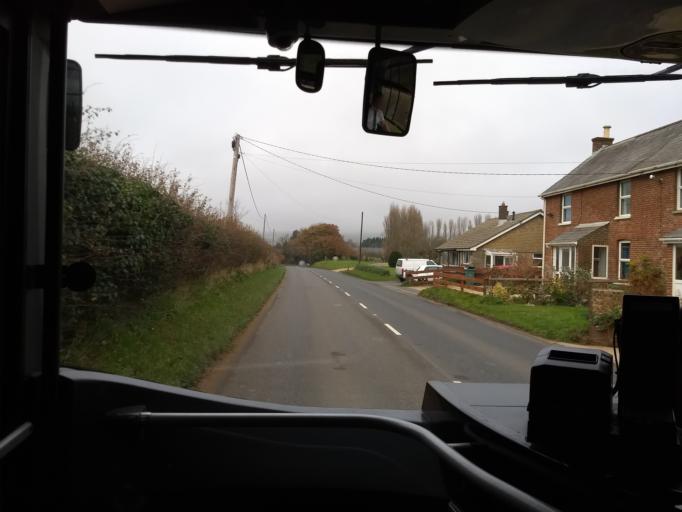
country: GB
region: England
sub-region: Isle of Wight
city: Newchurch
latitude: 50.6627
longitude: -1.2310
